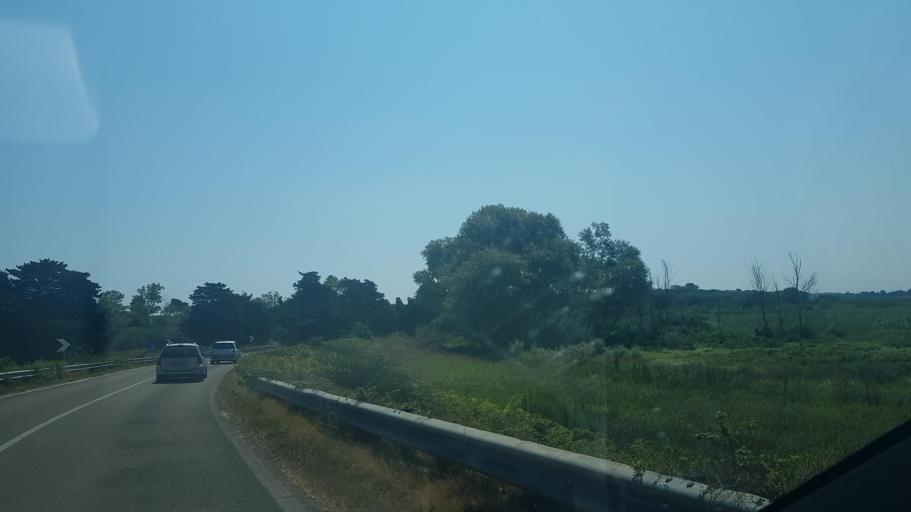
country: IT
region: Apulia
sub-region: Provincia di Lecce
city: Borgagne
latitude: 40.2250
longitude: 18.4375
